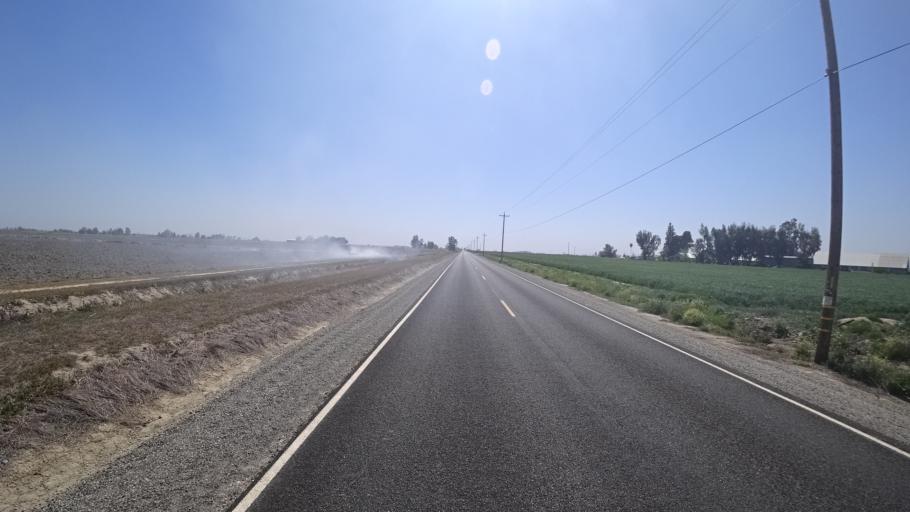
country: US
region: California
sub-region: Glenn County
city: Willows
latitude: 39.5351
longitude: -122.1368
